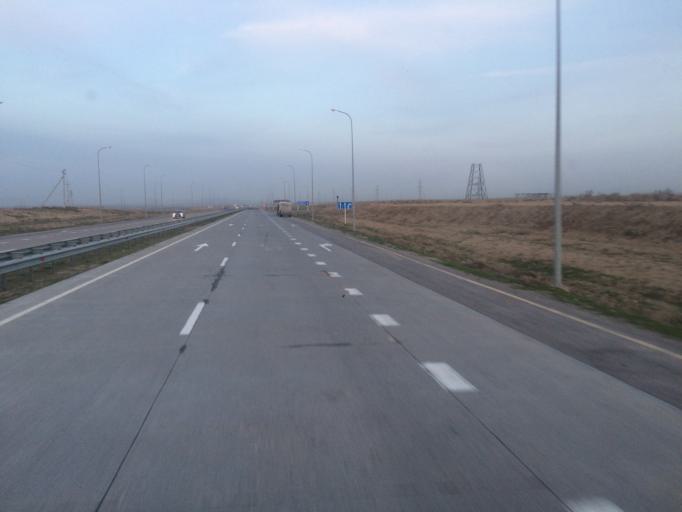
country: KZ
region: Ongtustik Qazaqstan
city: Shymkent
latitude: 42.4526
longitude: 69.6273
